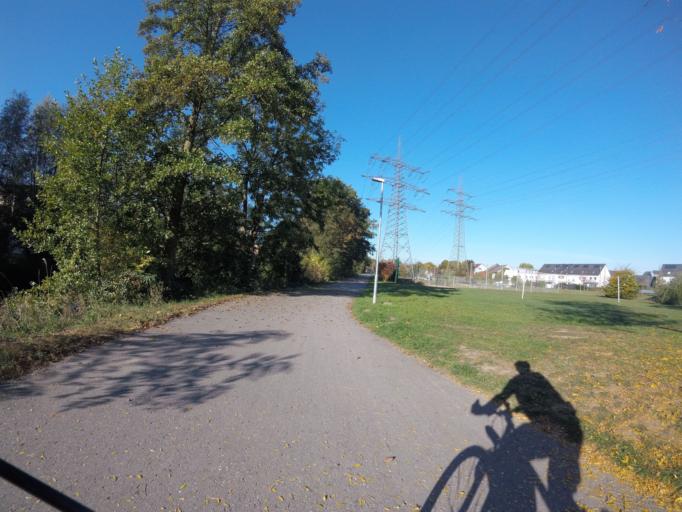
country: DE
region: Baden-Wuerttemberg
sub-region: Karlsruhe Region
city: Eggenstein-Leopoldshafen
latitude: 49.0886
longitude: 8.4059
